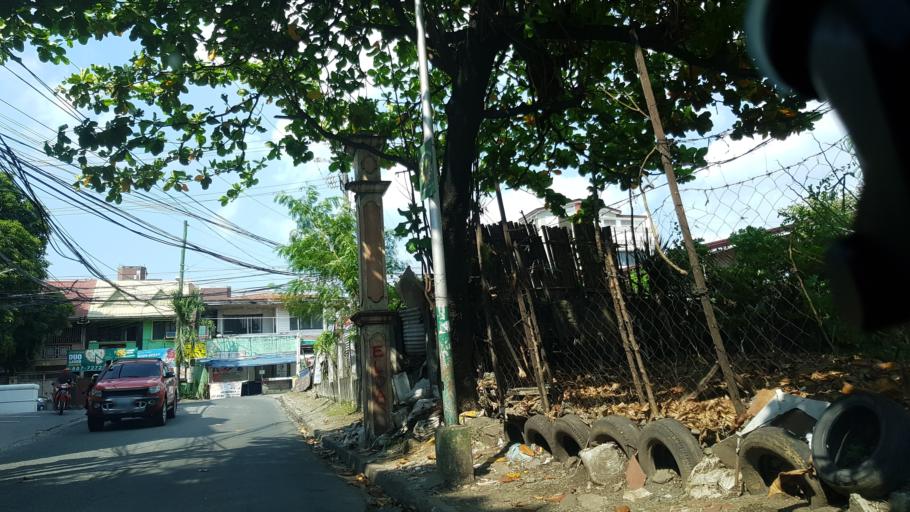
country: PH
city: Sambayanihan People's Village
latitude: 14.4734
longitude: 121.0248
